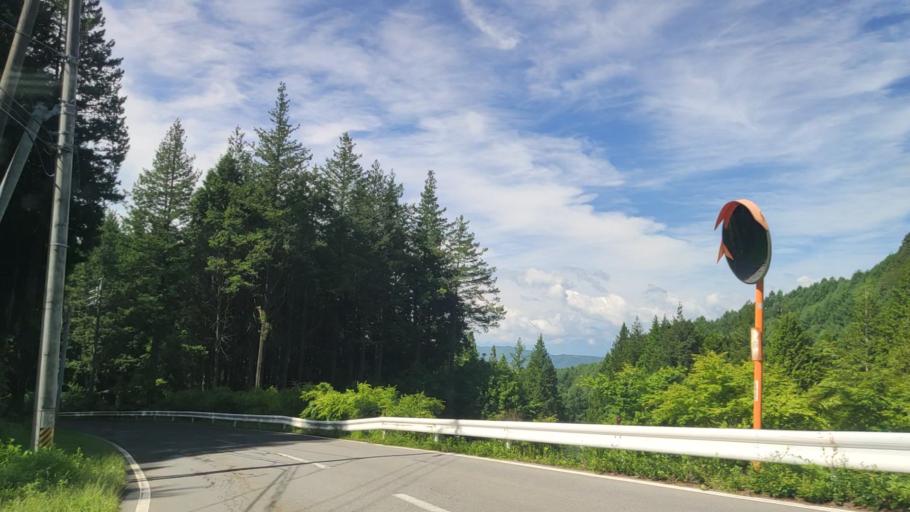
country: JP
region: Nagano
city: Suwa
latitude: 36.0751
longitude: 138.1375
